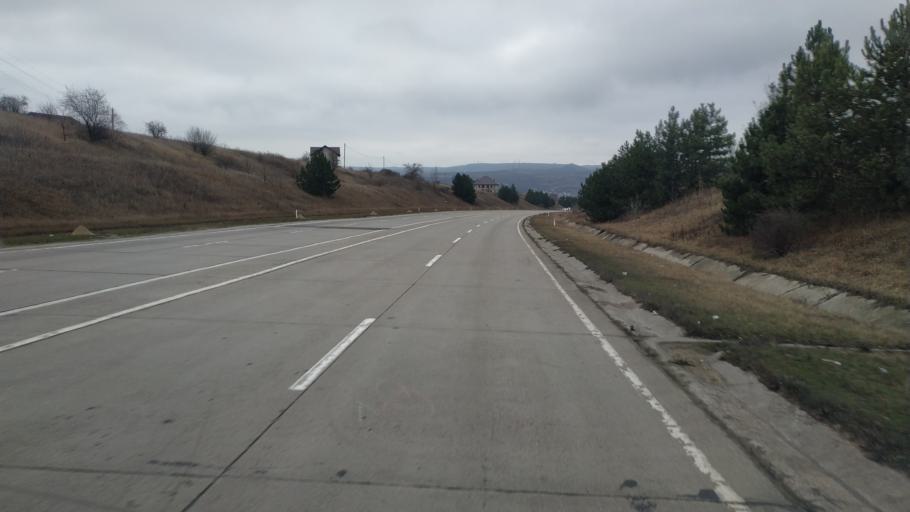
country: MD
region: Chisinau
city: Chisinau
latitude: 46.9278
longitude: 28.8693
